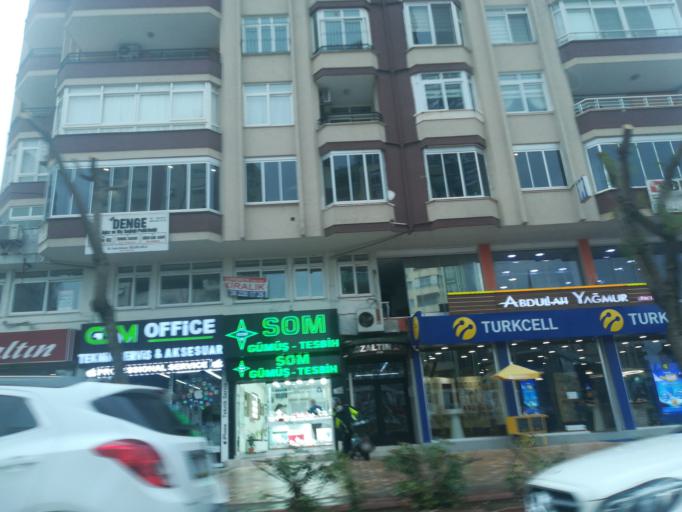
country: TR
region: Adana
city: Adana
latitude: 37.0467
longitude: 35.3026
